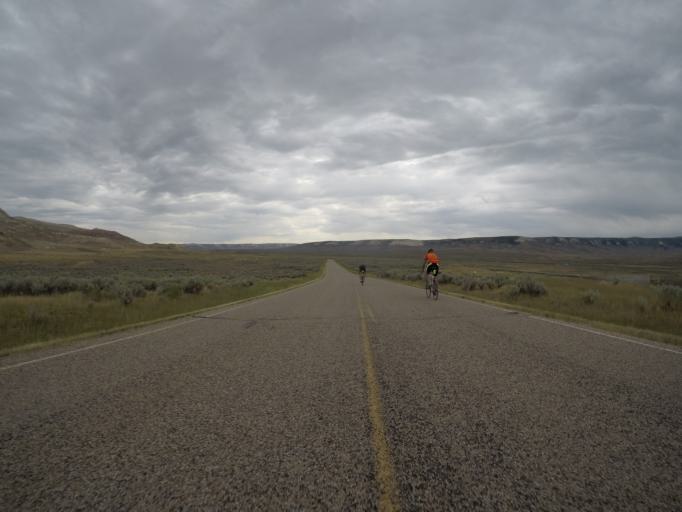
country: US
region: Wyoming
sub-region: Lincoln County
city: Kemmerer
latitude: 41.8273
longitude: -110.7677
